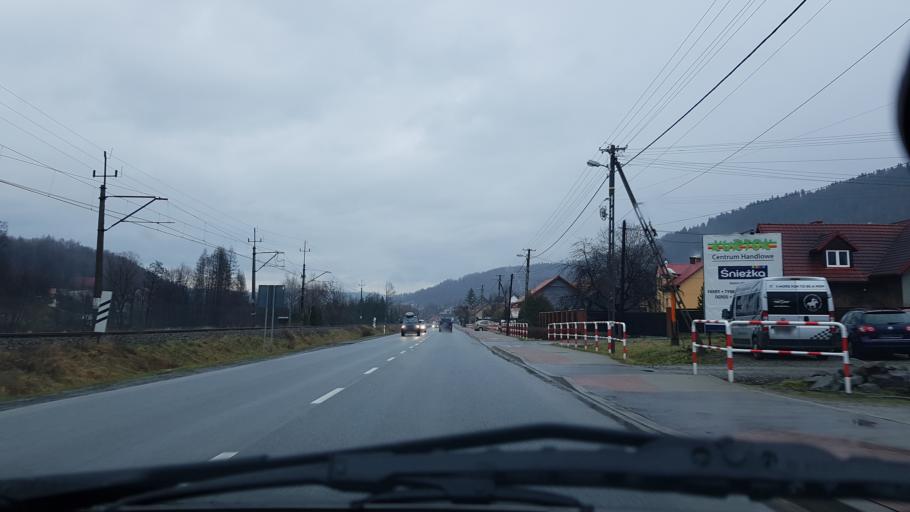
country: PL
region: Lesser Poland Voivodeship
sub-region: Powiat suski
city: Stryszawa
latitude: 49.7362
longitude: 19.5539
